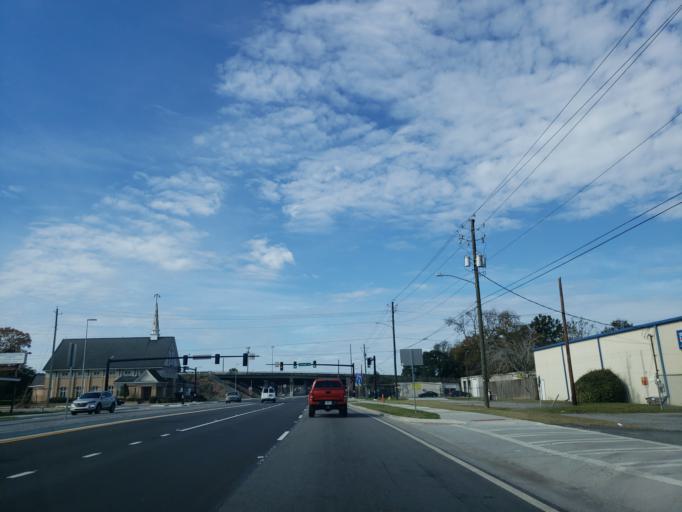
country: US
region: Georgia
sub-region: Chatham County
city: Savannah
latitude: 32.0902
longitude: -81.1249
